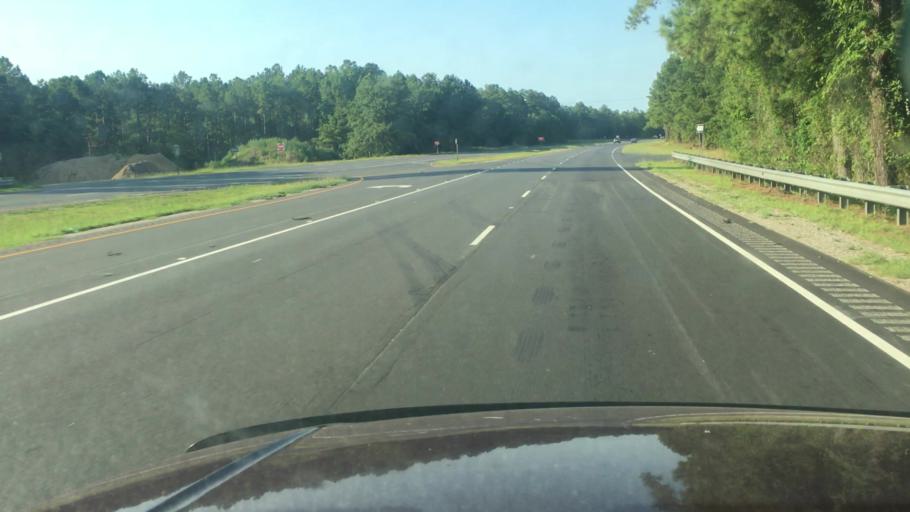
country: US
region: North Carolina
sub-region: Robeson County
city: Saint Pauls
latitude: 34.8587
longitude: -78.8497
